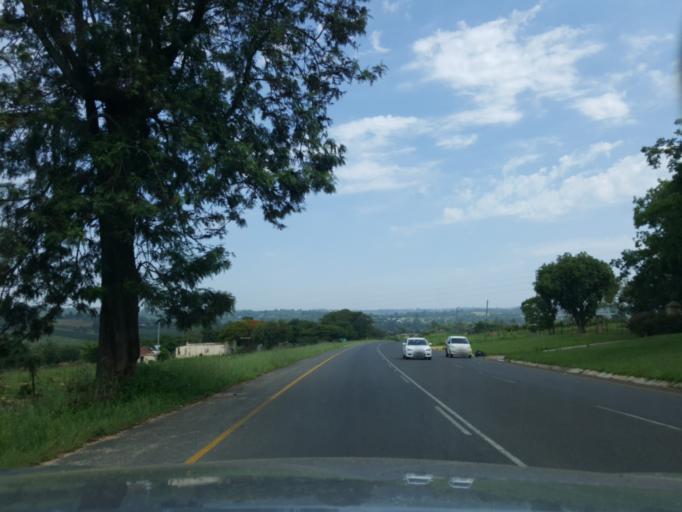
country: ZA
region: Mpumalanga
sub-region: Ehlanzeni District
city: White River
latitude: -25.3634
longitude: 31.0728
